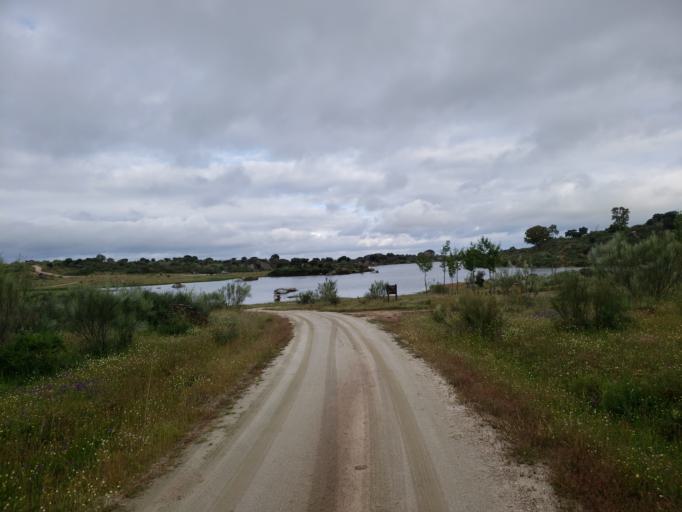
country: ES
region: Extremadura
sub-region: Provincia de Caceres
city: Malpartida de Caceres
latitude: 39.4253
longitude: -6.4843
